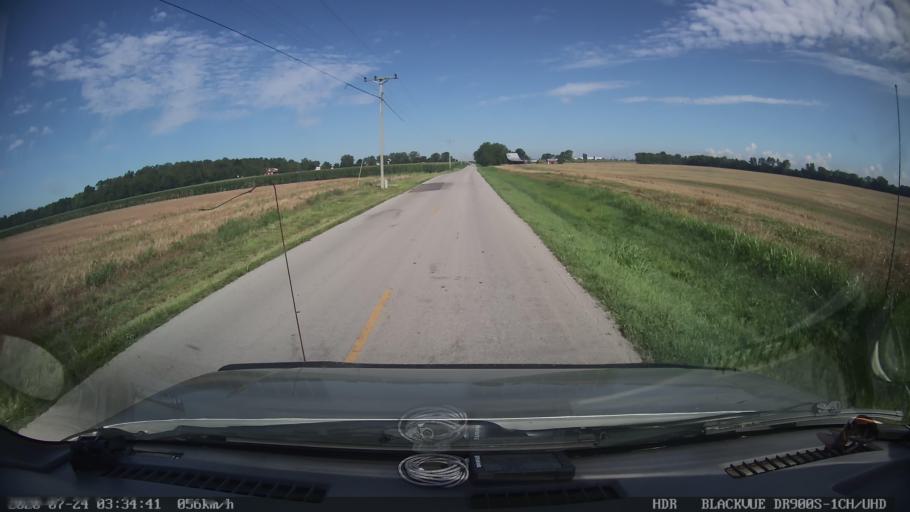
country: US
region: Kentucky
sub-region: Todd County
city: Guthrie
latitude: 36.7085
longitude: -87.2219
